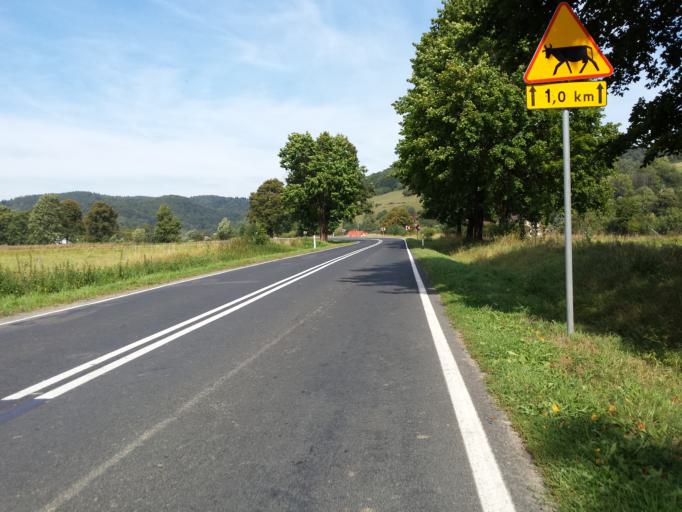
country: PL
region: Subcarpathian Voivodeship
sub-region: Powiat leski
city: Baligrod
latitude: 49.3543
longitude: 22.2866
